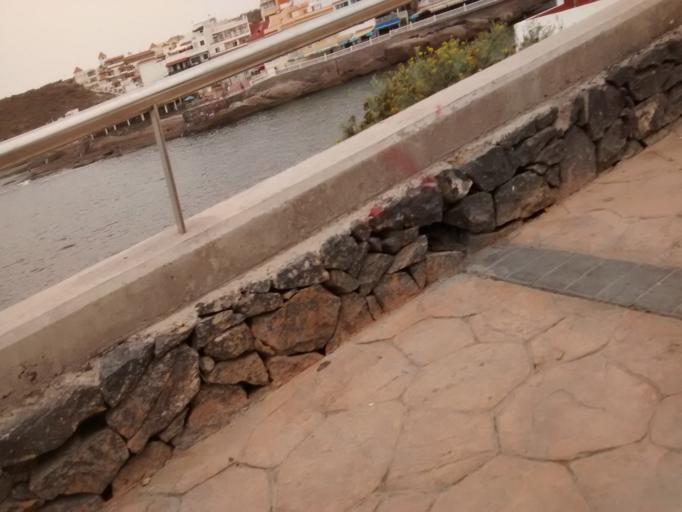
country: ES
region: Canary Islands
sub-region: Provincia de Santa Cruz de Tenerife
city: Adeje
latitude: 28.0997
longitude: -16.7557
